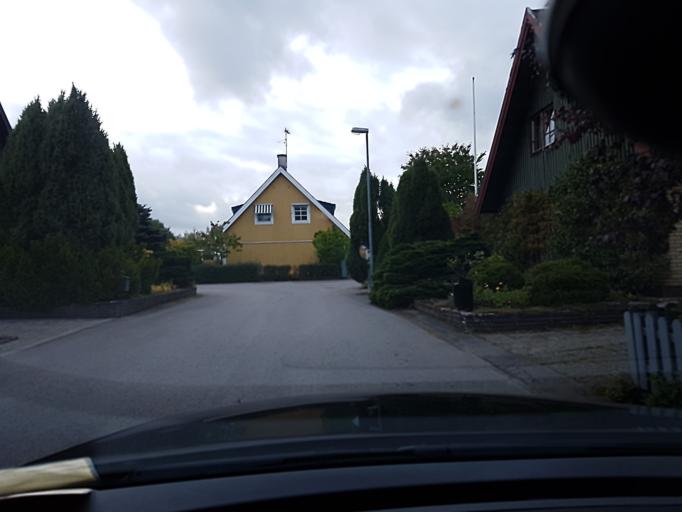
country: SE
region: Kronoberg
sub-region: Vaxjo Kommun
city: Vaexjoe
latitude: 56.8449
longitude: 14.8201
